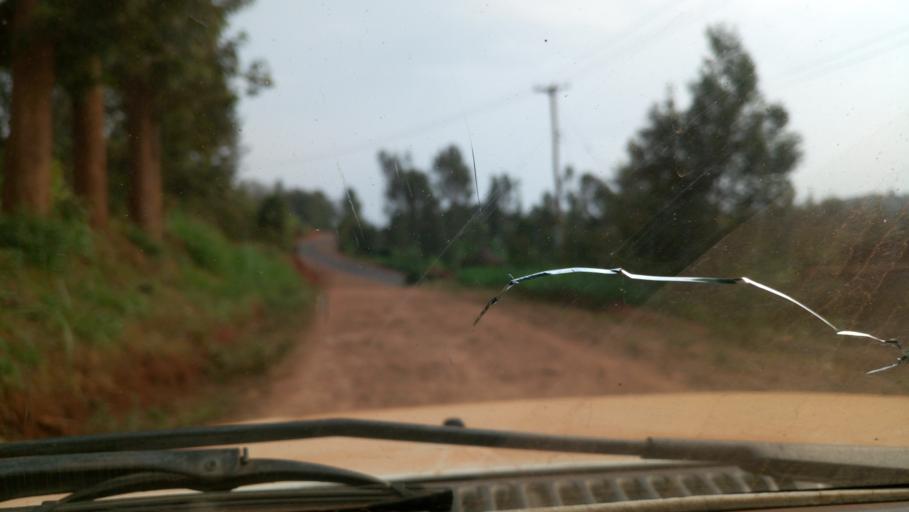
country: KE
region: Murang'a District
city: Kangema
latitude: -0.7825
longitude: 36.9909
